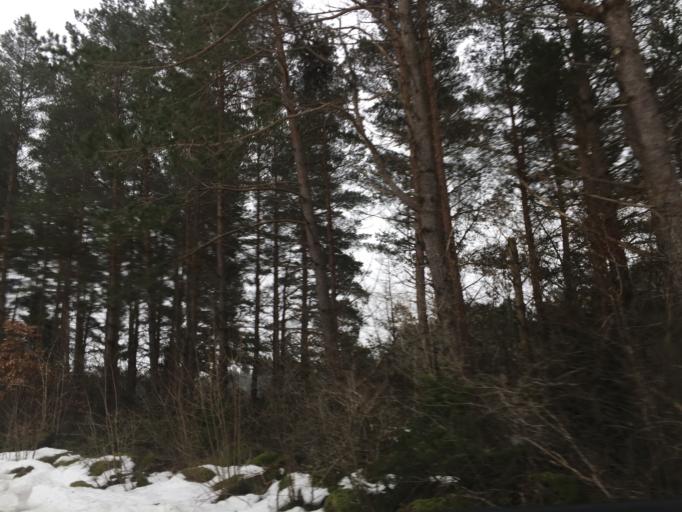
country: EE
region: Saare
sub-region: Orissaare vald
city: Orissaare
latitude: 58.4163
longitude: 22.8242
